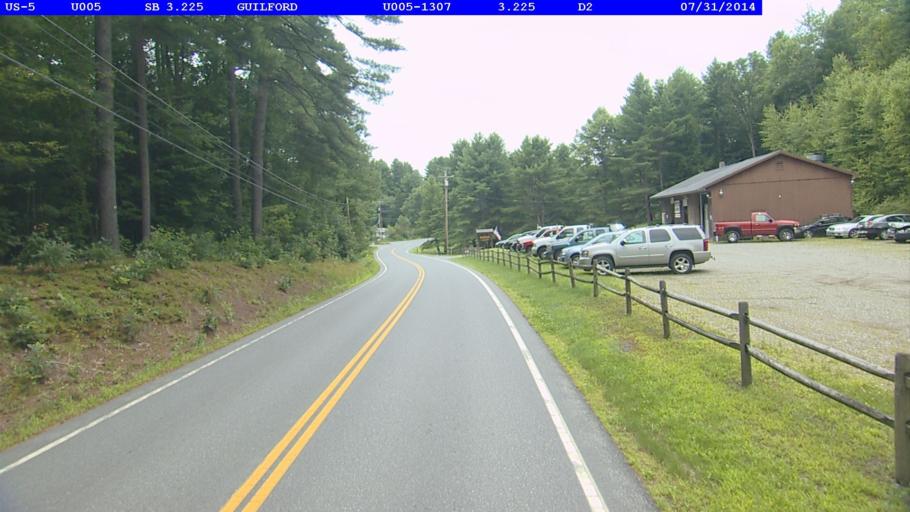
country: US
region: Vermont
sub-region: Windham County
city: Brattleboro
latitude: 42.7756
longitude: -72.5679
